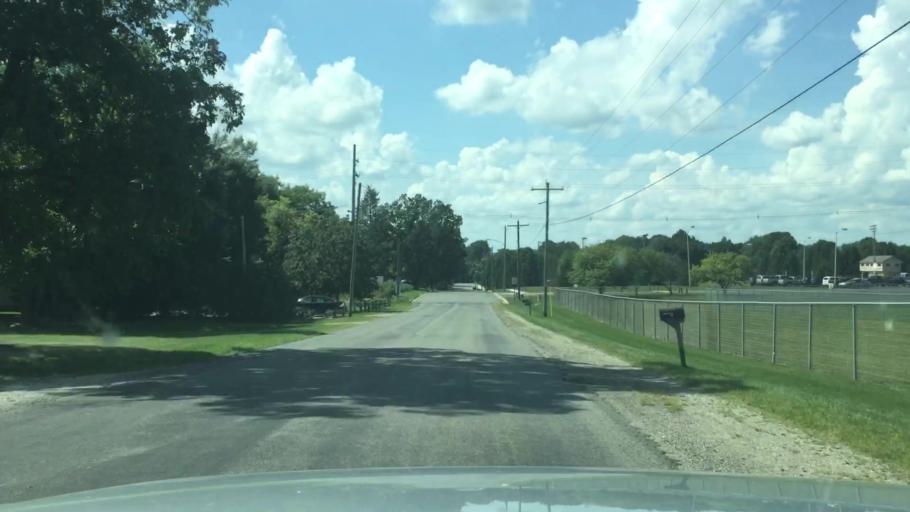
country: US
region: Michigan
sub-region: Lenawee County
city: Clinton
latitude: 42.0723
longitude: -83.9609
